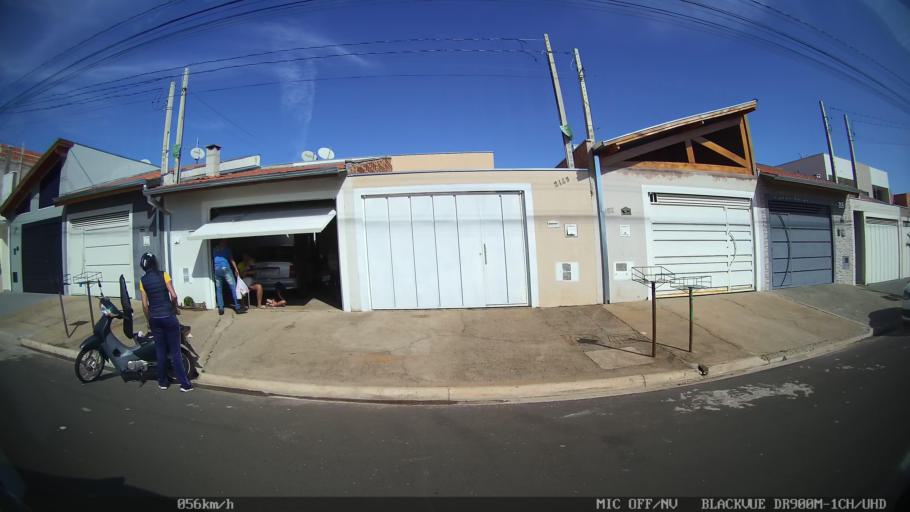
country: BR
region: Sao Paulo
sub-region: Franca
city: Franca
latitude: -20.5064
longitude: -47.4380
